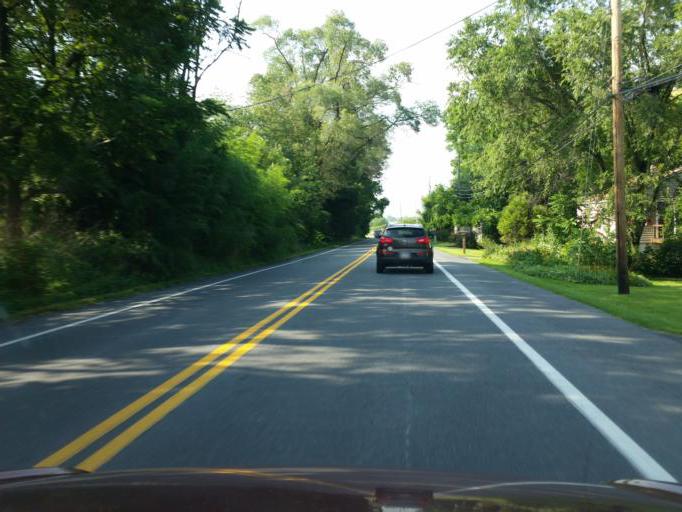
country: US
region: Pennsylvania
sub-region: Dauphin County
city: Hershey
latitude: 40.2465
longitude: -76.6256
